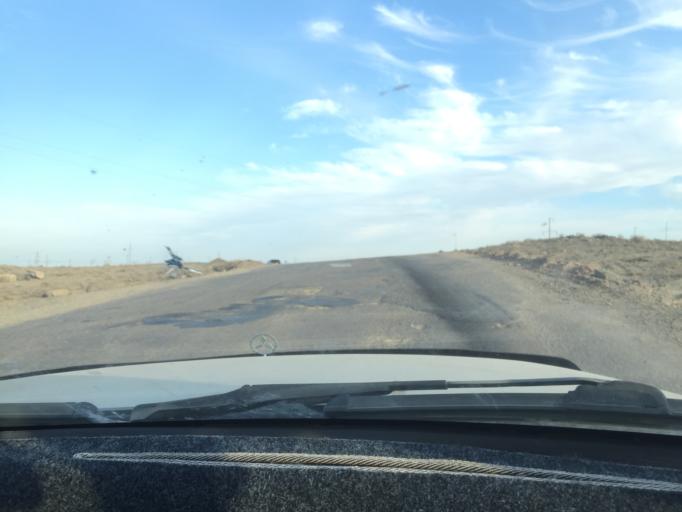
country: KZ
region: Almaty Oblysy
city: Ulken
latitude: 45.2060
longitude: 73.8827
